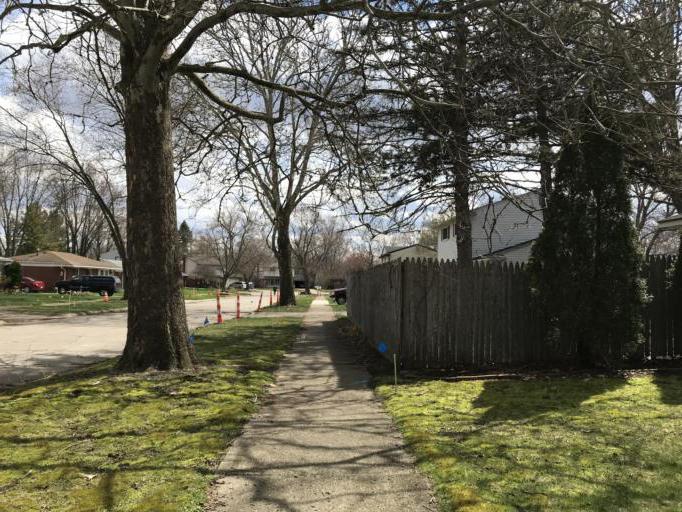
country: US
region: Michigan
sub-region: Oakland County
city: Farmington
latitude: 42.4654
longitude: -83.3443
